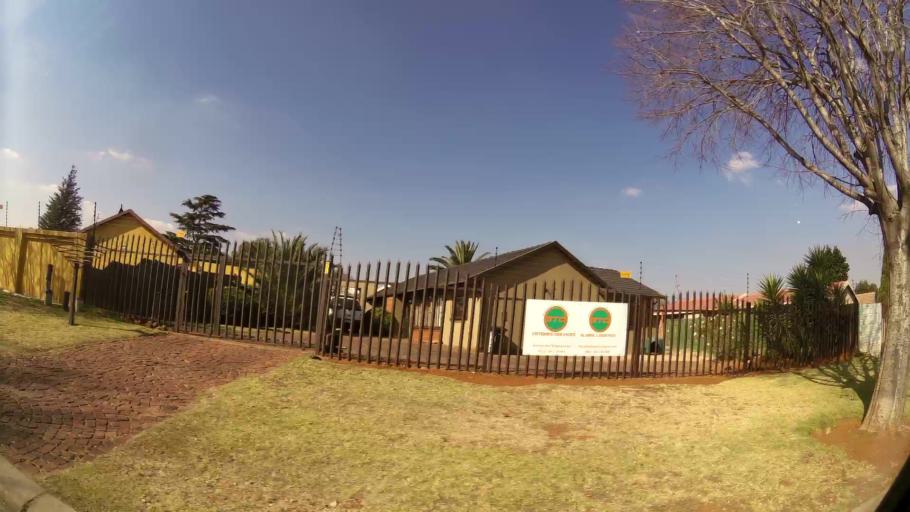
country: ZA
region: Gauteng
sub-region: Ekurhuleni Metropolitan Municipality
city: Benoni
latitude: -26.2422
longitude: 28.3111
